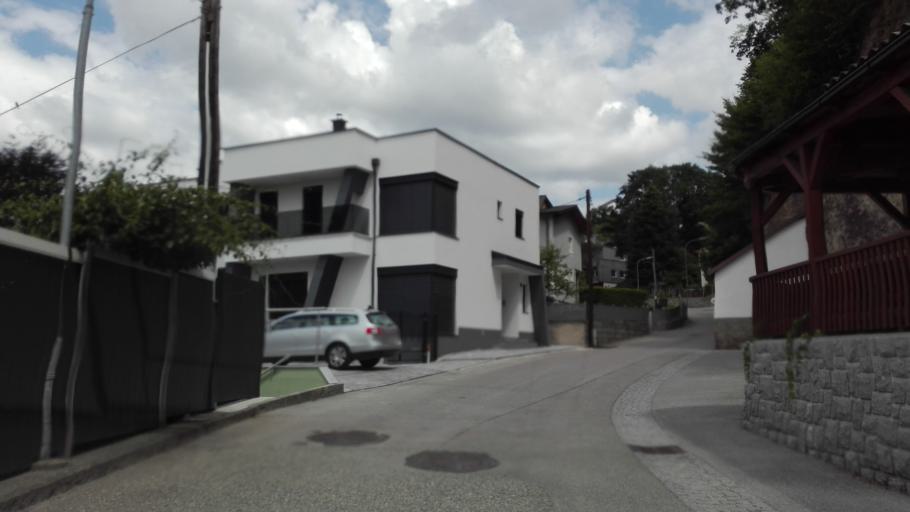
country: AT
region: Upper Austria
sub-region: Politischer Bezirk Perg
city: Perg
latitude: 48.2523
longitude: 14.6323
